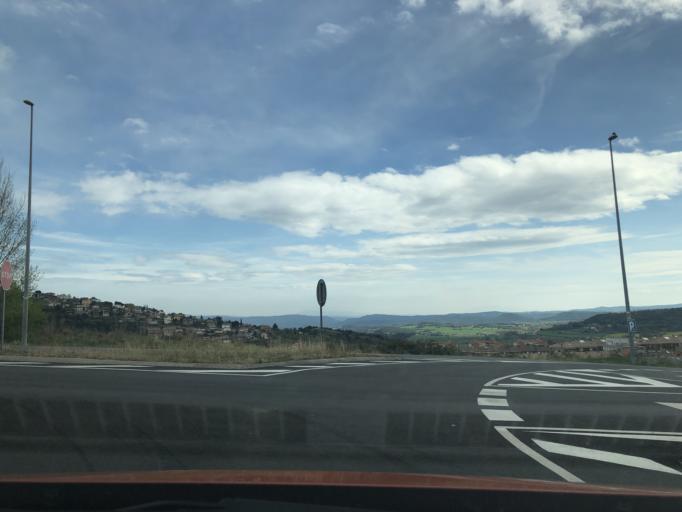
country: ES
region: Catalonia
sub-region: Provincia de Barcelona
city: Berga
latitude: 42.1082
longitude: 1.8544
